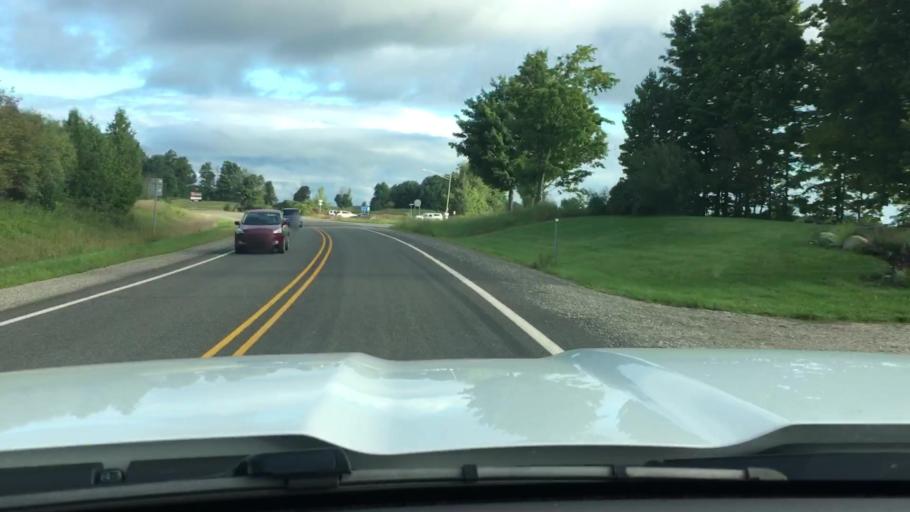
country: US
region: Michigan
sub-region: Lapeer County
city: Barnes Lake-Millers Lake
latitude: 43.3332
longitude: -83.3226
